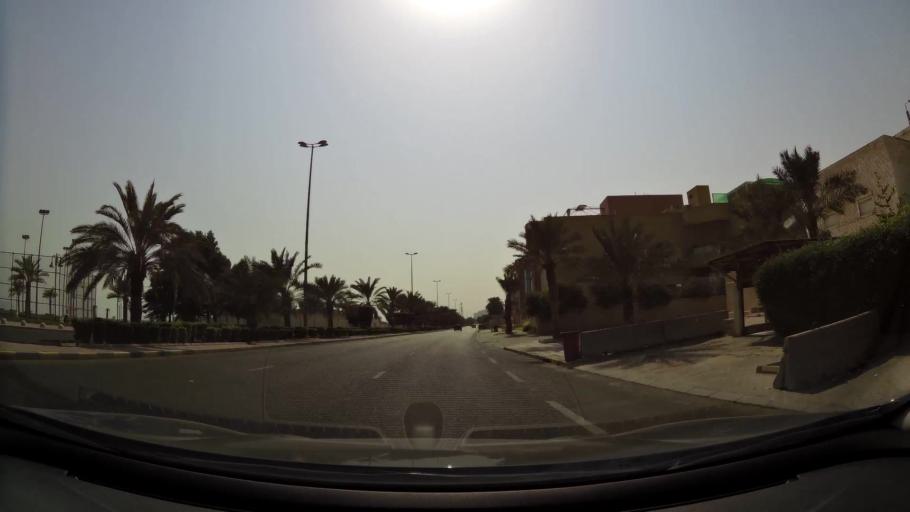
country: KW
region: Al Ahmadi
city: Al Fintas
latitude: 29.1765
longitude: 48.1222
